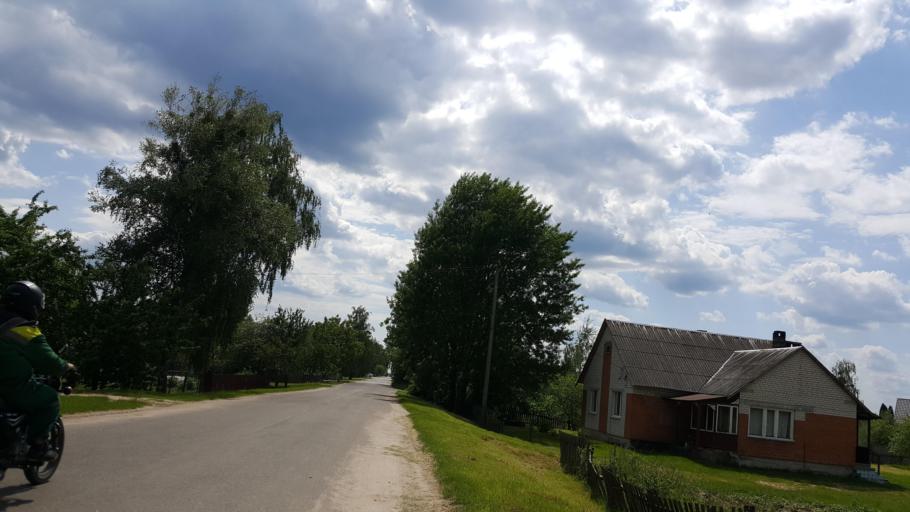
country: PL
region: Podlasie
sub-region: Powiat hajnowski
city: Bialowieza
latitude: 52.6733
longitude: 24.0887
